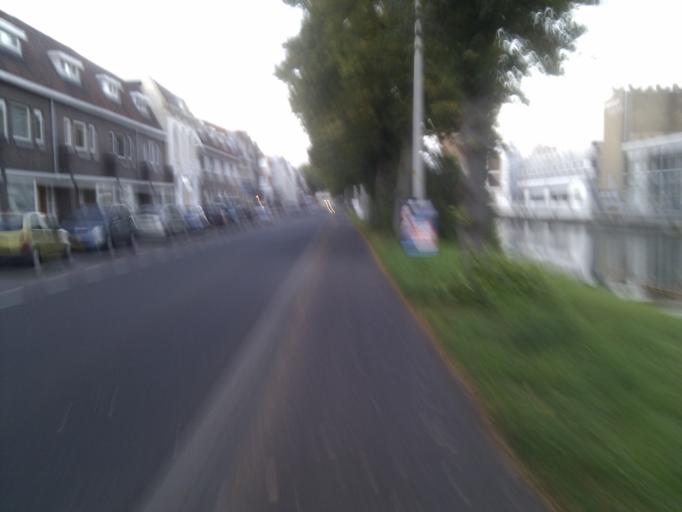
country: NL
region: Utrecht
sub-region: Gemeente Utrecht
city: Utrecht
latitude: 52.0740
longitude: 5.1194
